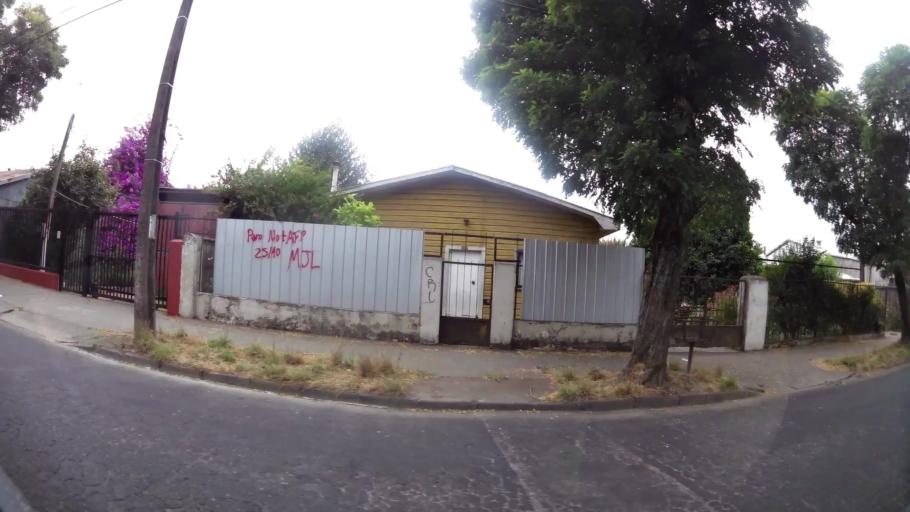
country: CL
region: Biobio
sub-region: Provincia de Concepcion
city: Concepcion
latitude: -36.8152
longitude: -73.0358
